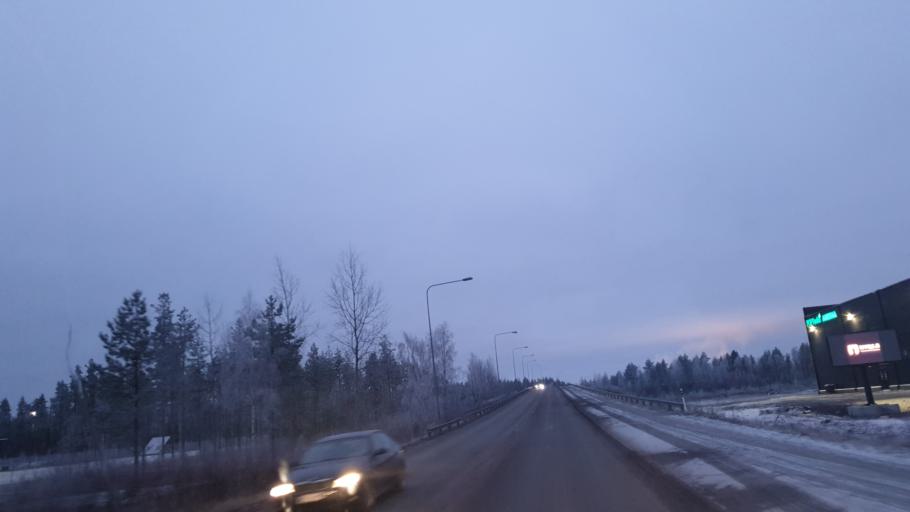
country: FI
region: Southern Ostrobothnia
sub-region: Seinaejoki
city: Nurmo
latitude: 62.7764
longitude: 22.8920
